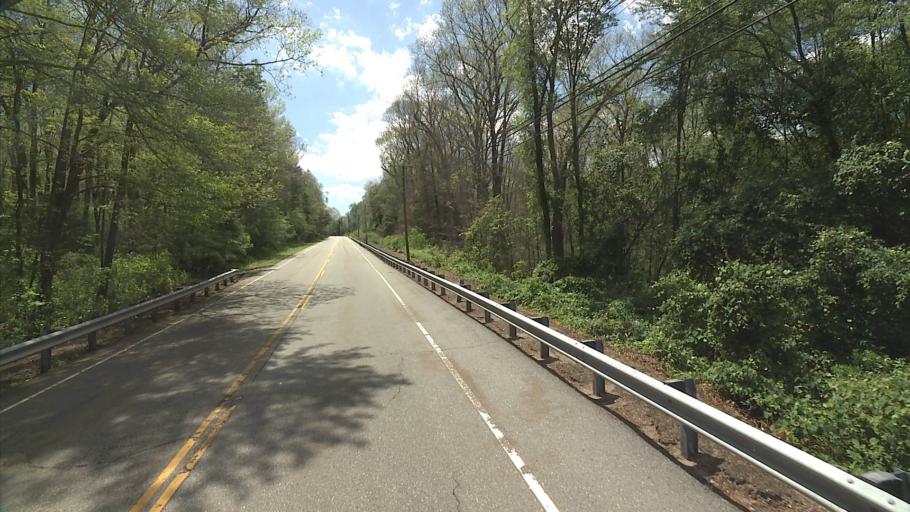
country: US
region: Connecticut
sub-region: Middlesex County
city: Moodus
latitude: 41.5174
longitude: -72.4876
